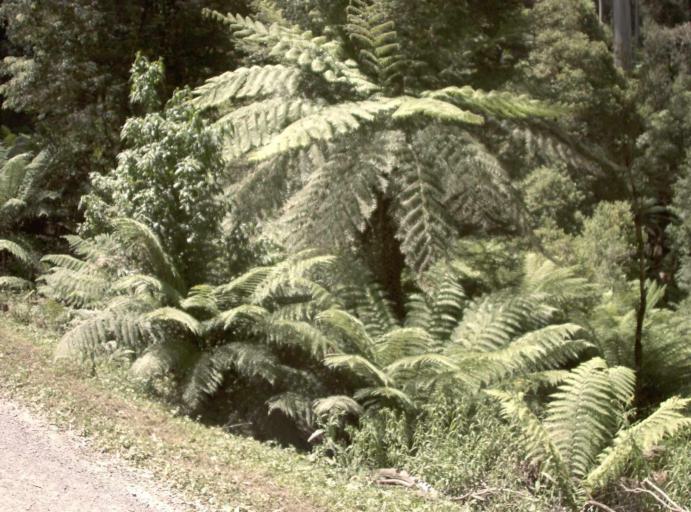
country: AU
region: Victoria
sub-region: Yarra Ranges
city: Millgrove
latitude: -37.6856
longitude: 145.7203
